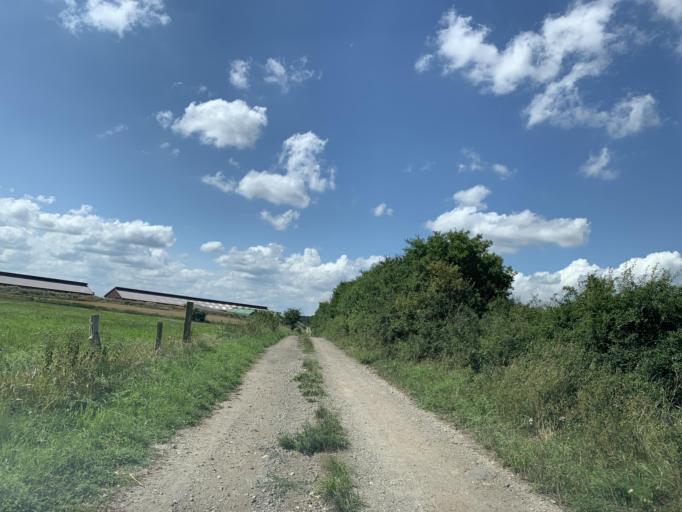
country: DE
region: Mecklenburg-Vorpommern
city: Blankensee
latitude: 53.3983
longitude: 13.2849
